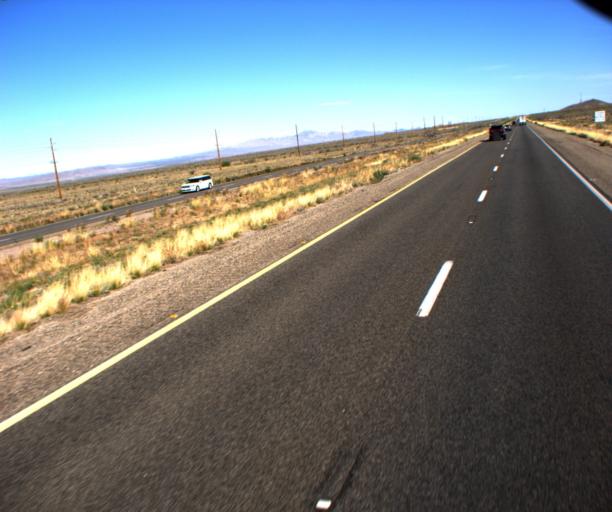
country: US
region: Arizona
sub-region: Mohave County
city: Golden Valley
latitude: 35.4019
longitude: -114.2627
